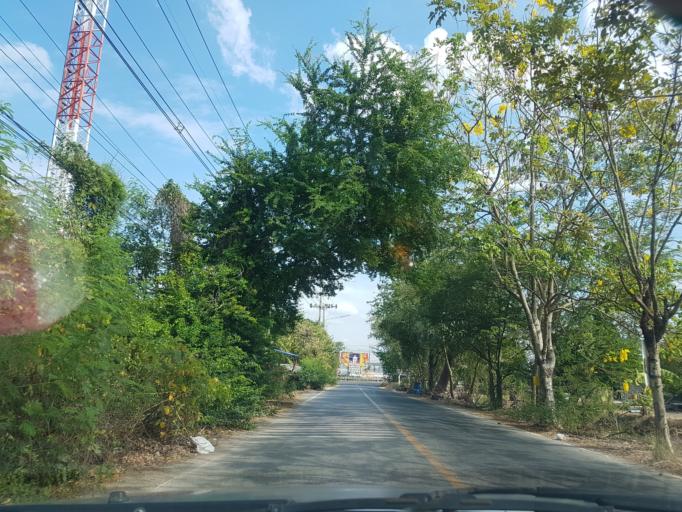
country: TH
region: Pathum Thani
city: Nong Suea
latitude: 14.1354
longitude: 100.8907
